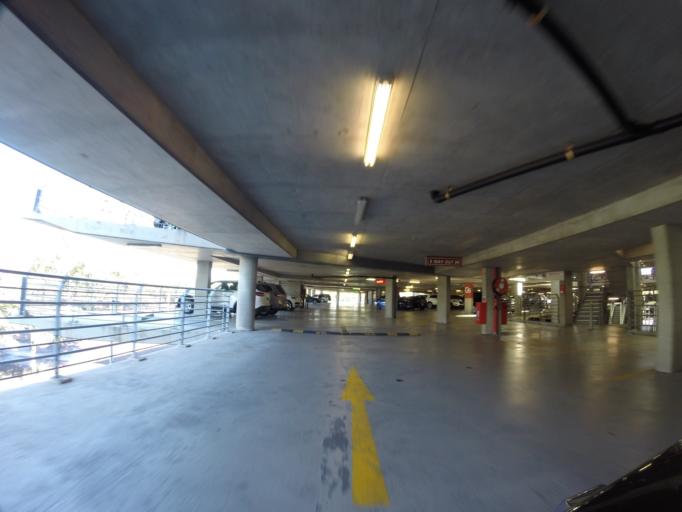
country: AU
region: New South Wales
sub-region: Canada Bay
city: Concord West
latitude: -33.8460
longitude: 151.0618
